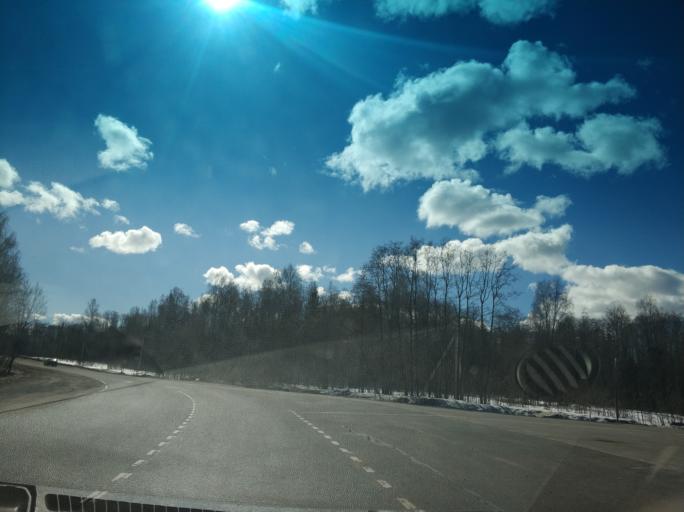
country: RU
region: Leningrad
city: Sosnovo
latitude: 60.4434
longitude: 30.2347
